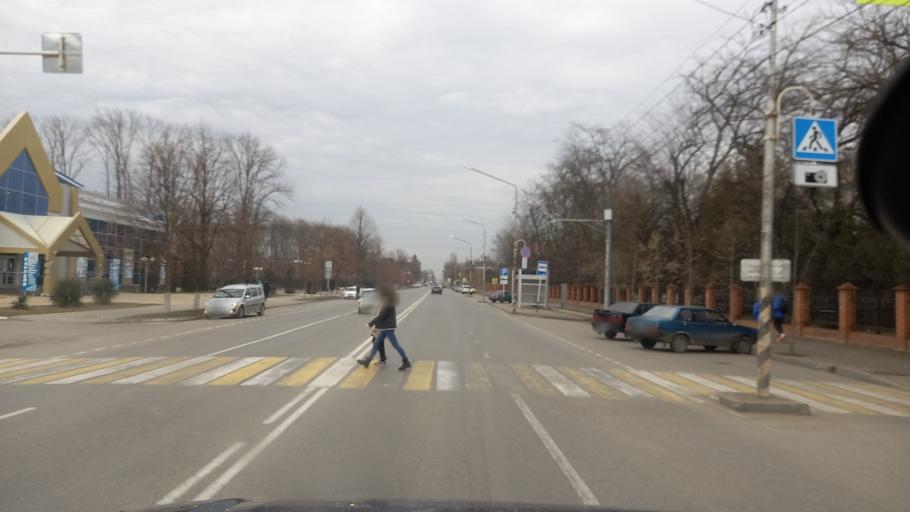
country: RU
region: Adygeya
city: Maykop
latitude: 44.5965
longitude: 40.1092
